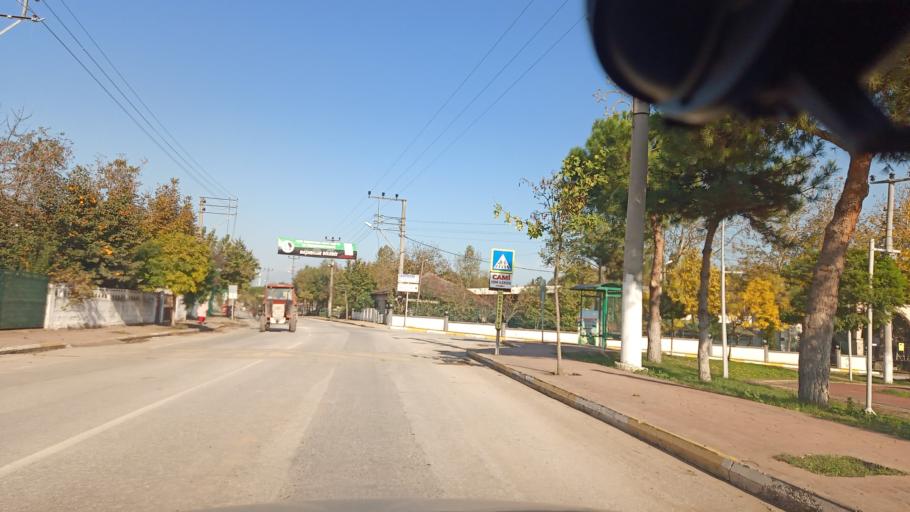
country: TR
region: Sakarya
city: Sogutlu
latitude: 40.8947
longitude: 30.4688
